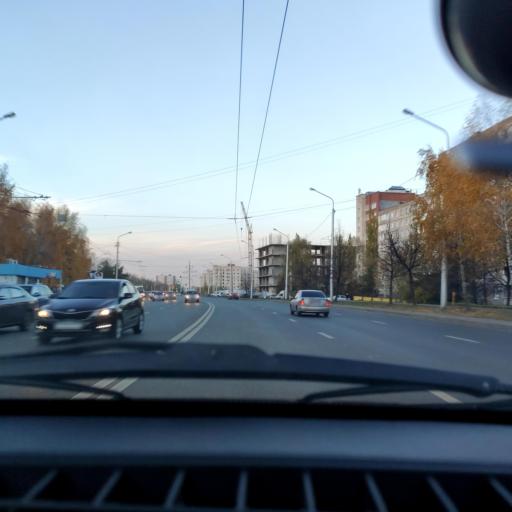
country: RU
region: Bashkortostan
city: Ufa
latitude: 54.7705
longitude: 56.0330
